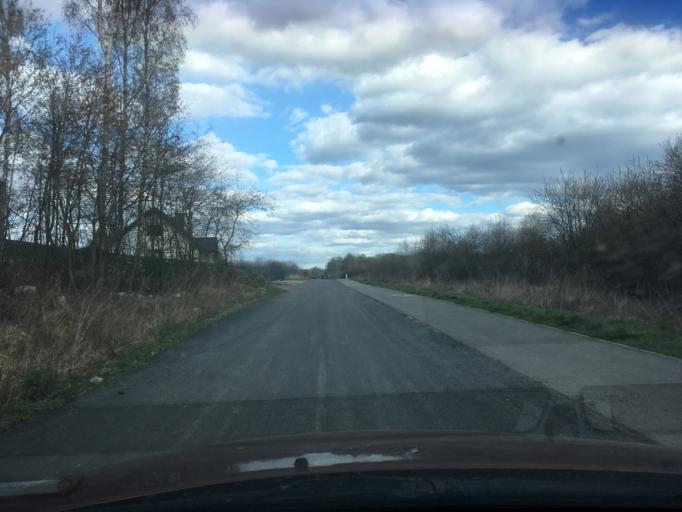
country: PL
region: Lower Silesian Voivodeship
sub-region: Powiat zgorzelecki
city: Zgorzelec
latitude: 51.1252
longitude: 15.0053
